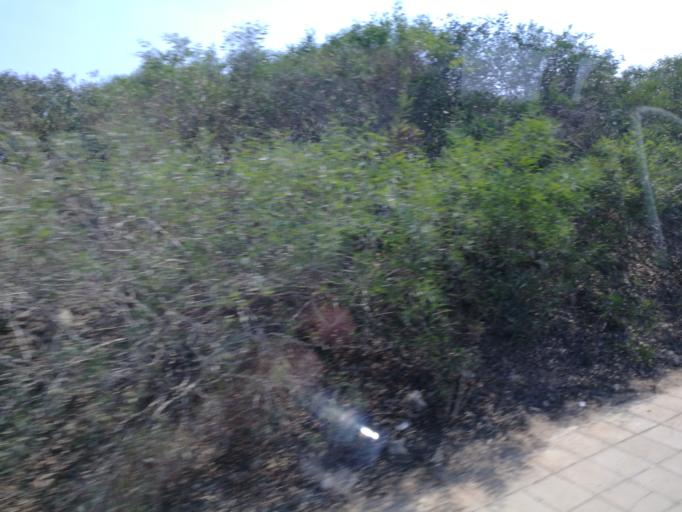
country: CY
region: Ammochostos
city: Protaras
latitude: 35.0279
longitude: 34.0291
